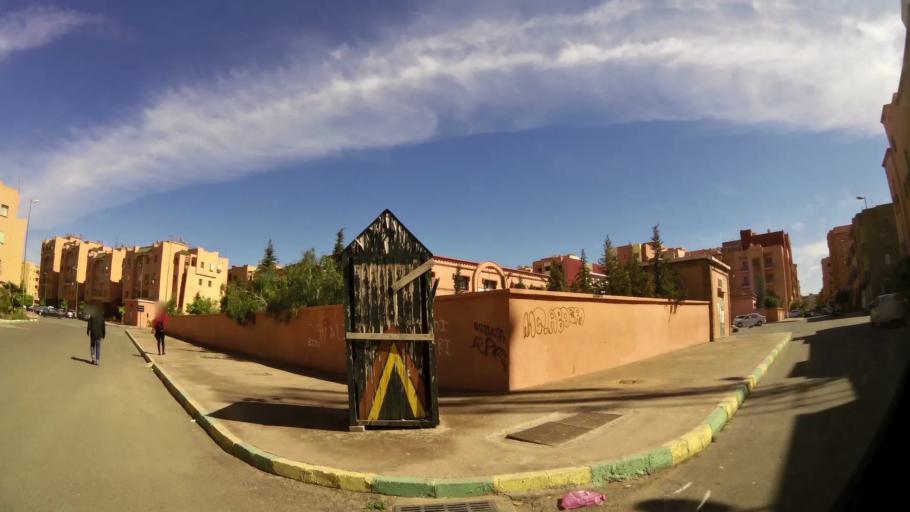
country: MA
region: Marrakech-Tensift-Al Haouz
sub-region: Marrakech
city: Marrakesh
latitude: 31.6745
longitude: -8.0189
